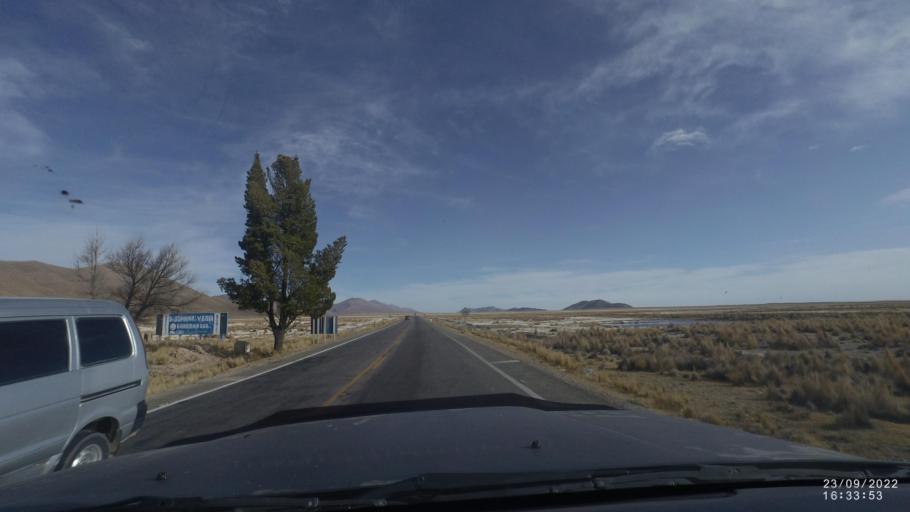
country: BO
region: Oruro
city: Machacamarca
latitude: -18.1806
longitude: -67.0161
